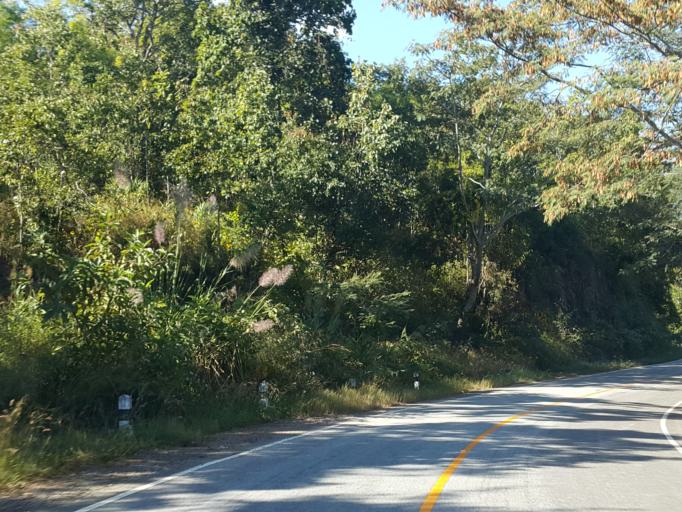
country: TH
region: Chiang Mai
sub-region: Amphoe Chiang Dao
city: Chiang Dao
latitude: 19.5255
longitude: 98.8677
